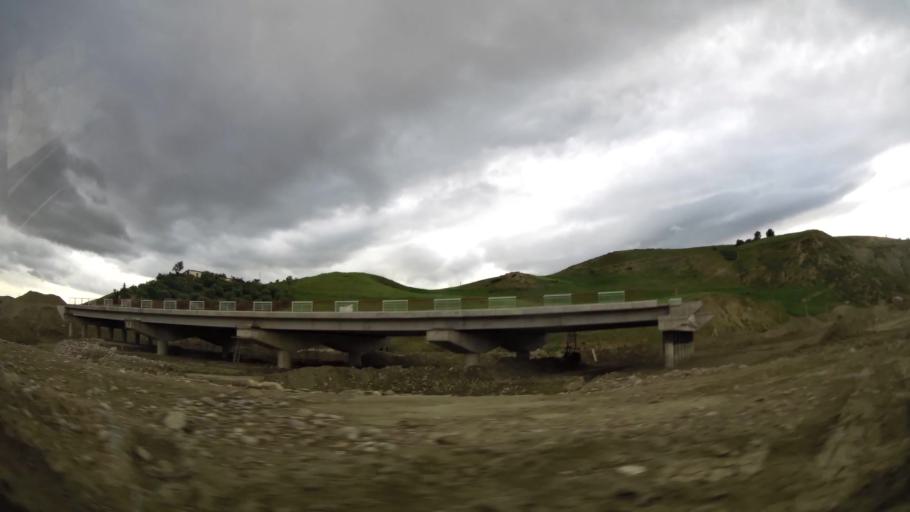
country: MA
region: Taza-Al Hoceima-Taounate
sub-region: Taza
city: Taza
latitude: 34.3430
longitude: -3.9279
